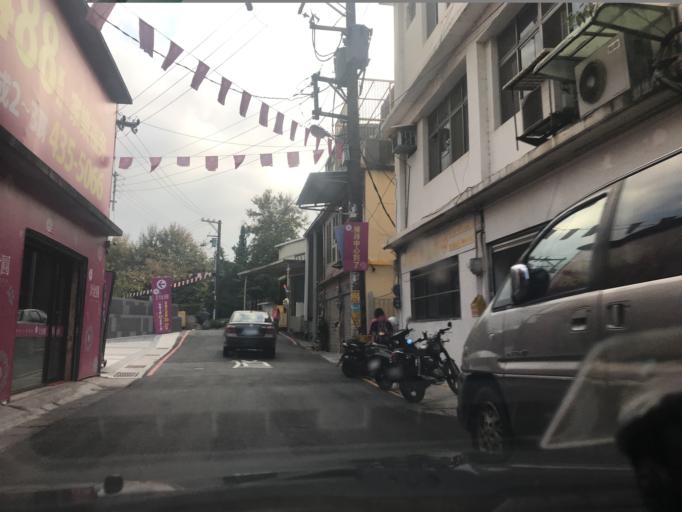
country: TW
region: Taiwan
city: Taoyuan City
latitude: 24.9654
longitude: 121.2350
